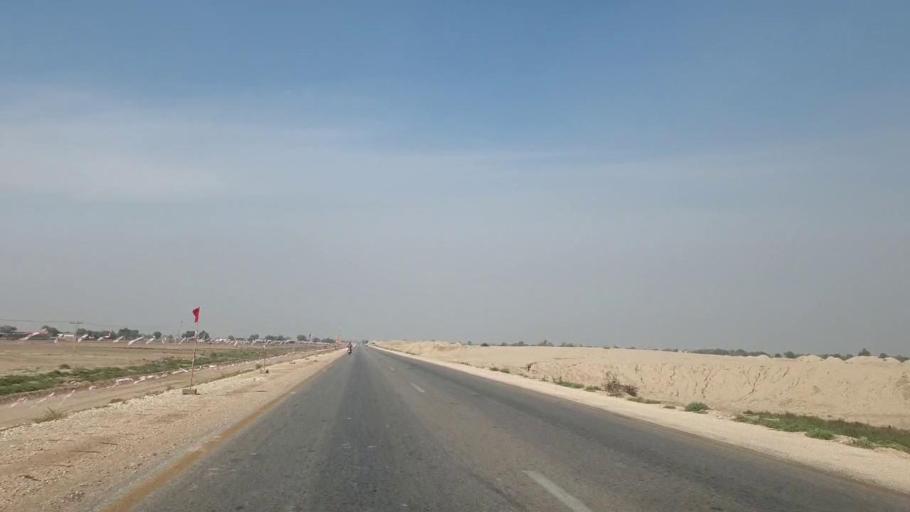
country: PK
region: Sindh
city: Sann
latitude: 25.9652
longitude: 68.1905
